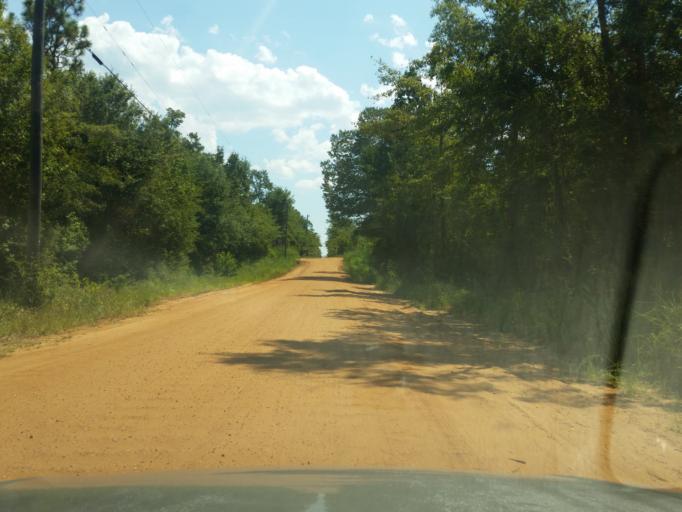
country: US
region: Florida
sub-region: Escambia County
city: Gonzalez
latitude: 30.6200
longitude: -87.2782
